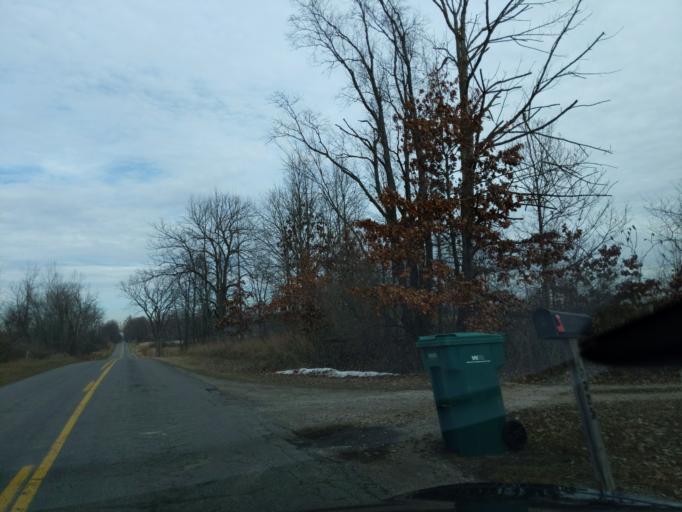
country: US
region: Michigan
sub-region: Ingham County
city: Leslie
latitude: 42.4852
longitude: -84.5022
